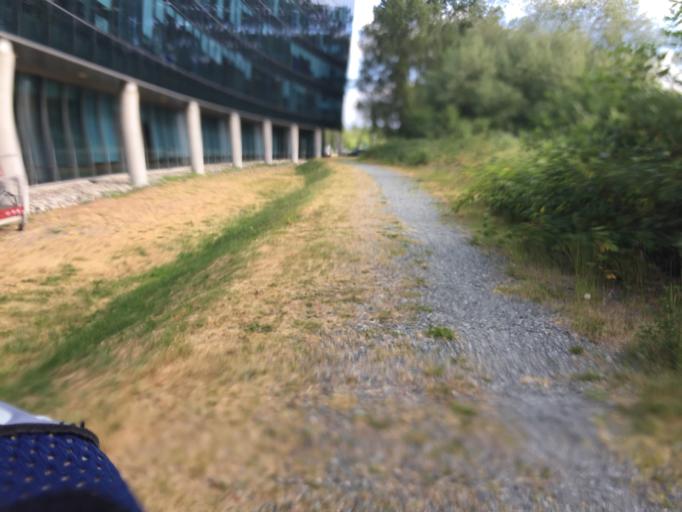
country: CA
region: British Columbia
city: Richmond
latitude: 49.1853
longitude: -123.1434
